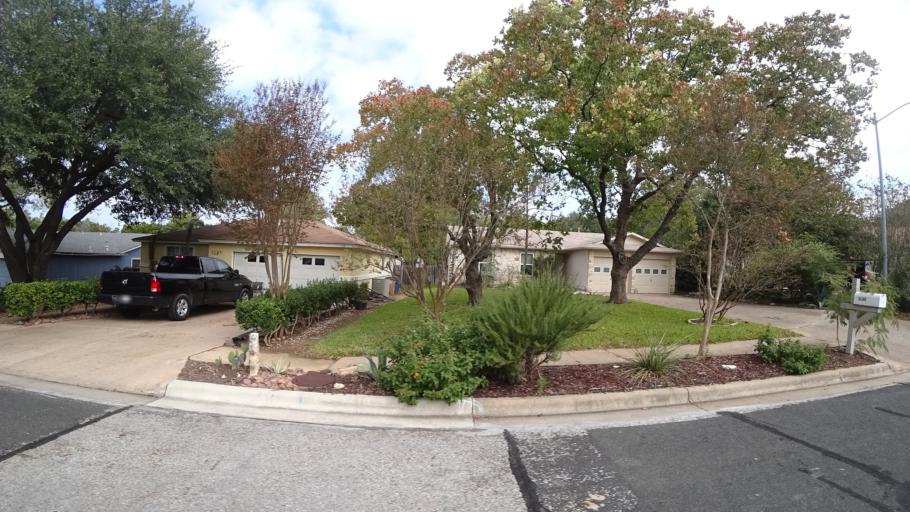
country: US
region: Texas
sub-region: Travis County
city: Shady Hollow
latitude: 30.2020
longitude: -97.8309
